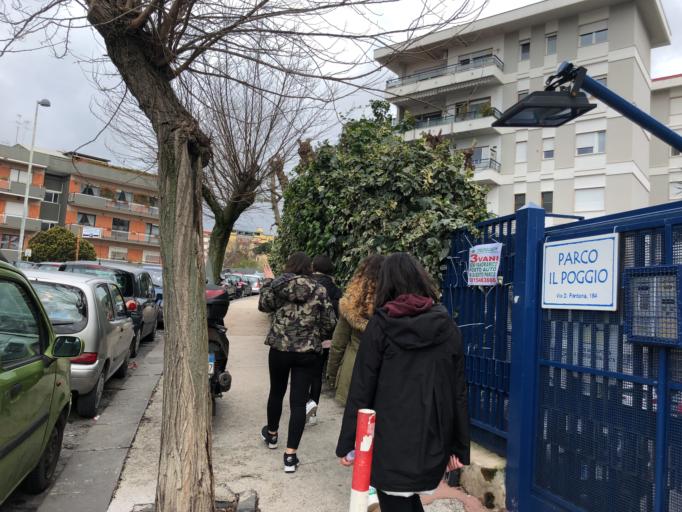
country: IT
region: Campania
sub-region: Provincia di Napoli
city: Napoli
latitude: 40.8587
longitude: 14.2248
